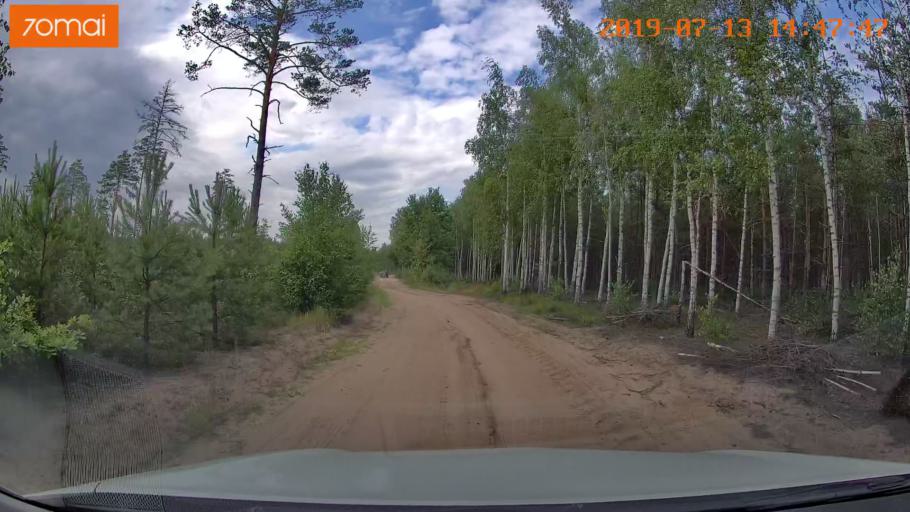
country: BY
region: Mogilev
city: Asipovichy
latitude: 53.2028
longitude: 28.7528
